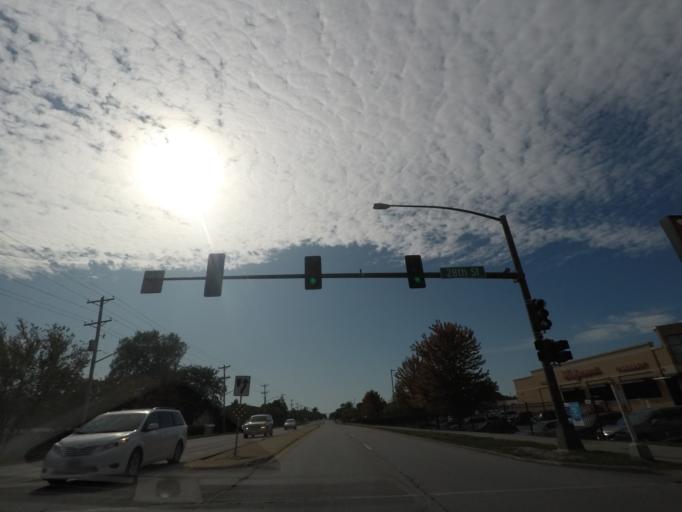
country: US
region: Iowa
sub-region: Story County
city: Ames
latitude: 42.0487
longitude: -93.6208
